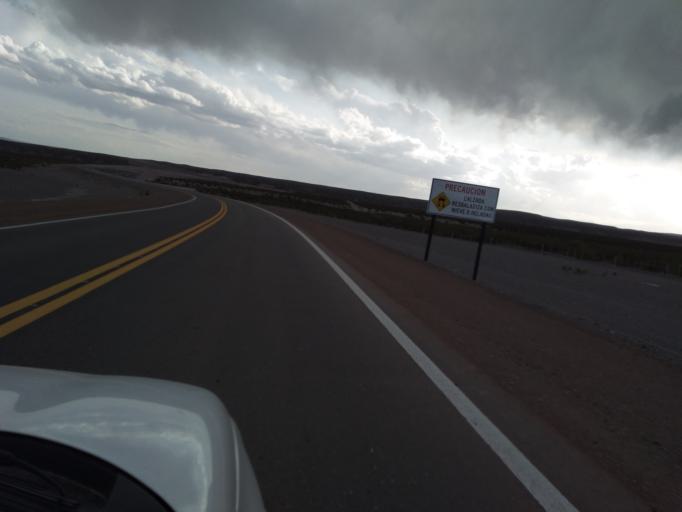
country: AR
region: Mendoza
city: La Consulta
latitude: -34.5455
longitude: -69.1647
